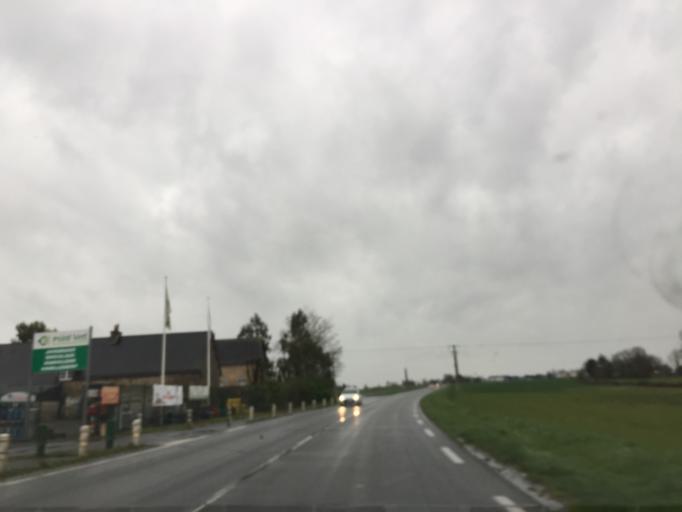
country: FR
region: Brittany
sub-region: Departement d'Ille-et-Vilaine
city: Fougeres
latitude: 48.3264
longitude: -1.1858
